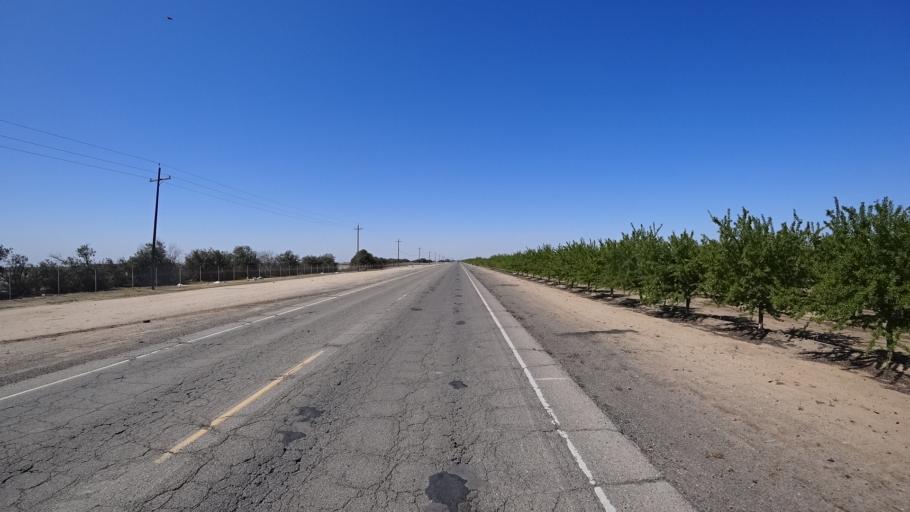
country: US
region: California
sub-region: Fresno County
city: West Park
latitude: 36.7063
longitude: -119.9003
